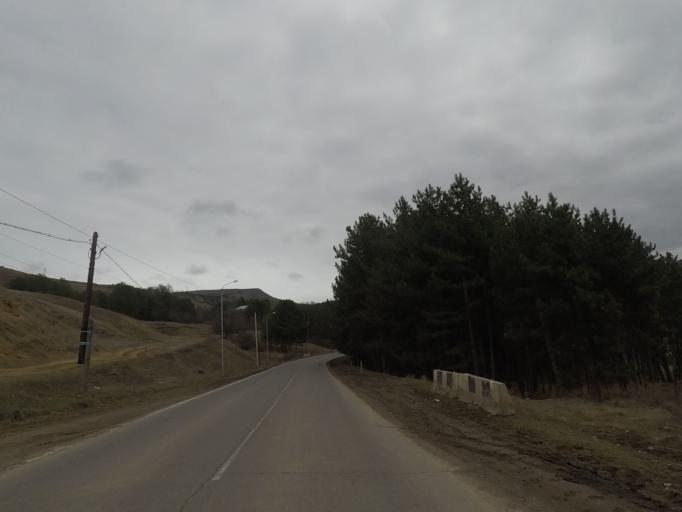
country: GE
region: Samtskhe-Javakheti
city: Aspindza
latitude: 41.5857
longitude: 43.2425
